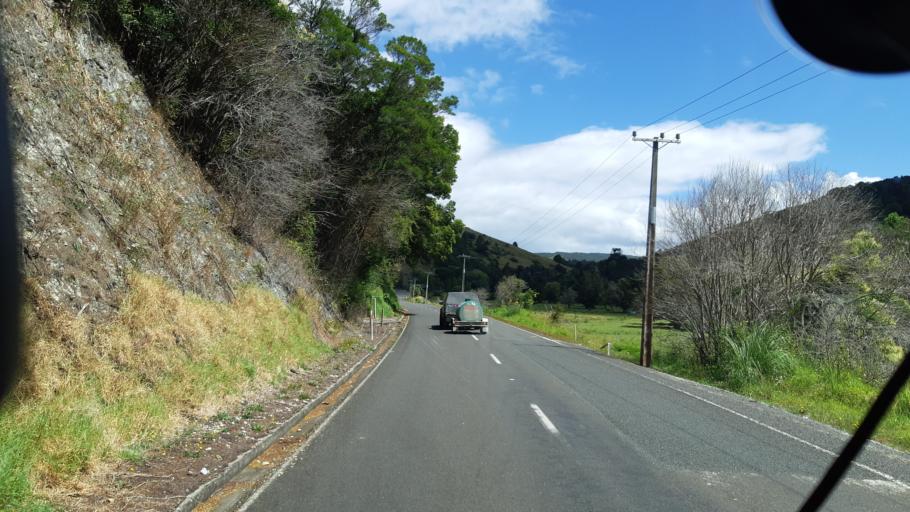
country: NZ
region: Northland
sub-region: Far North District
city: Taipa
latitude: -35.2707
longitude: 173.5062
